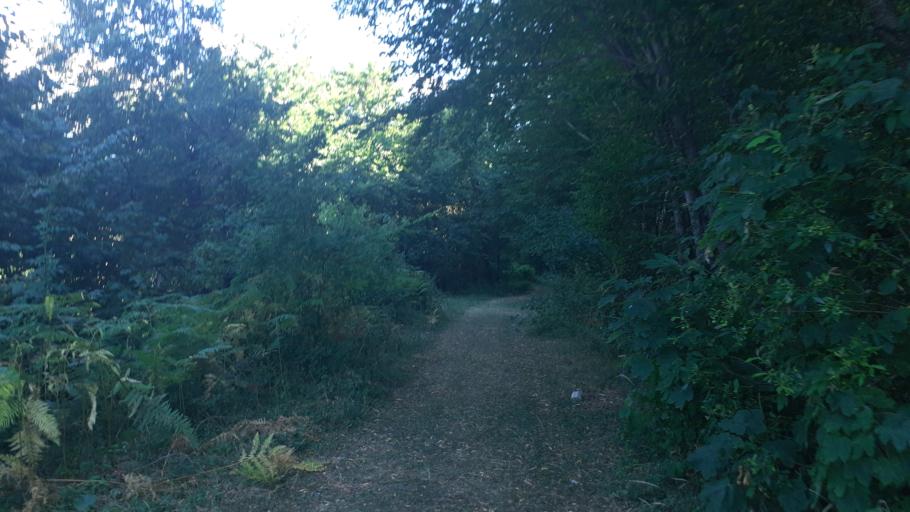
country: IT
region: Abruzzo
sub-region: Provincia di Pescara
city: Sant'Eufemia a Maiella
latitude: 42.1075
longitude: 14.0017
